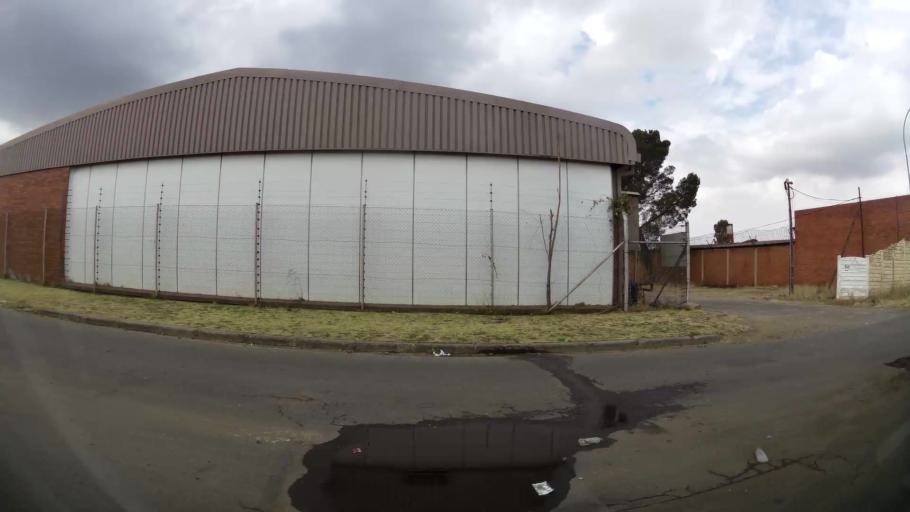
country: ZA
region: Orange Free State
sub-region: Mangaung Metropolitan Municipality
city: Bloemfontein
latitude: -29.1262
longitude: 26.2263
